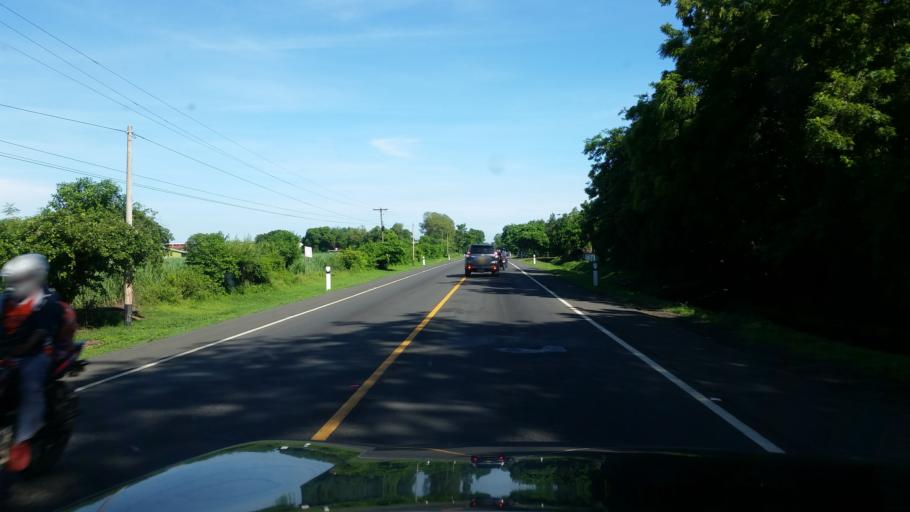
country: NI
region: Chinandega
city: Posoltega
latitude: 12.5550
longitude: -86.9441
